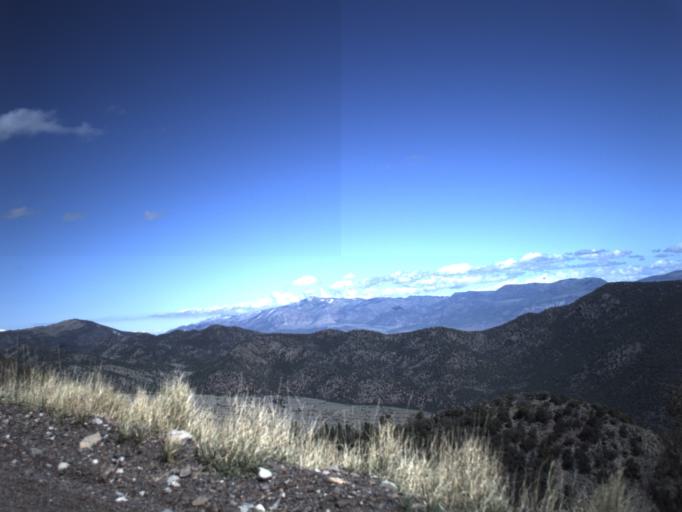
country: US
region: Utah
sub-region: Piute County
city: Junction
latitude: 38.2590
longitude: -112.3187
